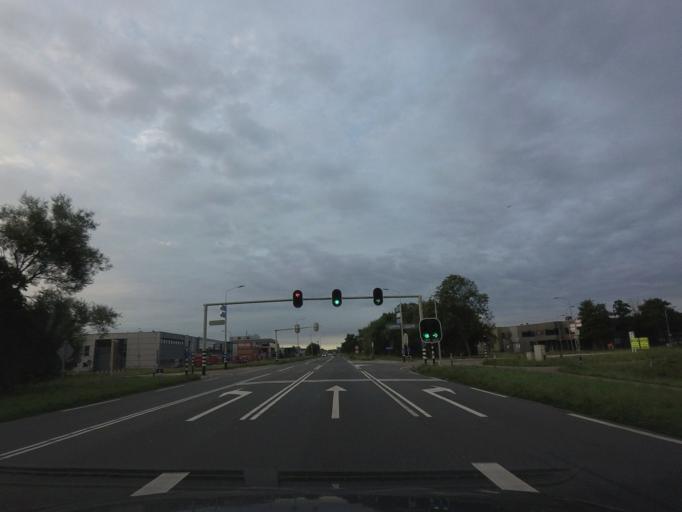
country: NL
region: North Holland
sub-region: Gemeente Zaanstad
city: Zaanstad
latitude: 52.5121
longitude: 4.7817
